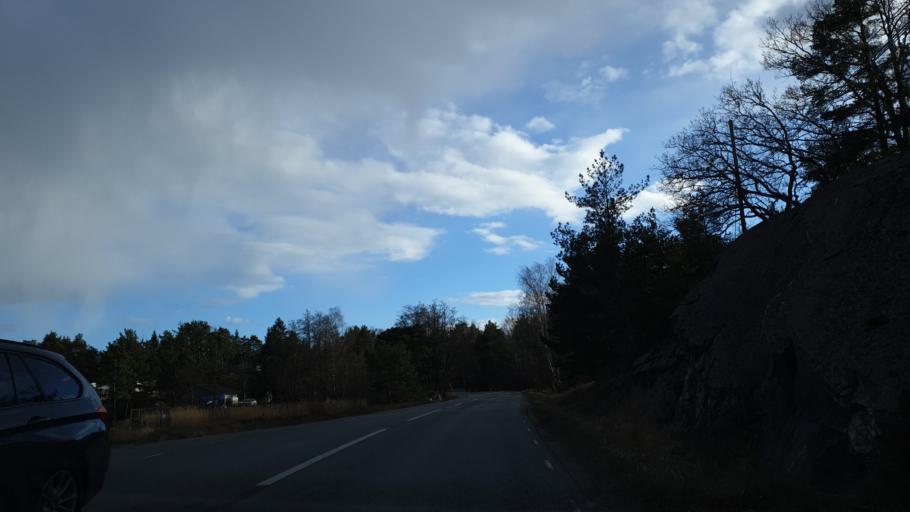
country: SE
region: Stockholm
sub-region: Varmdo Kommun
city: Holo
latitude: 59.3256
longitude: 18.7231
